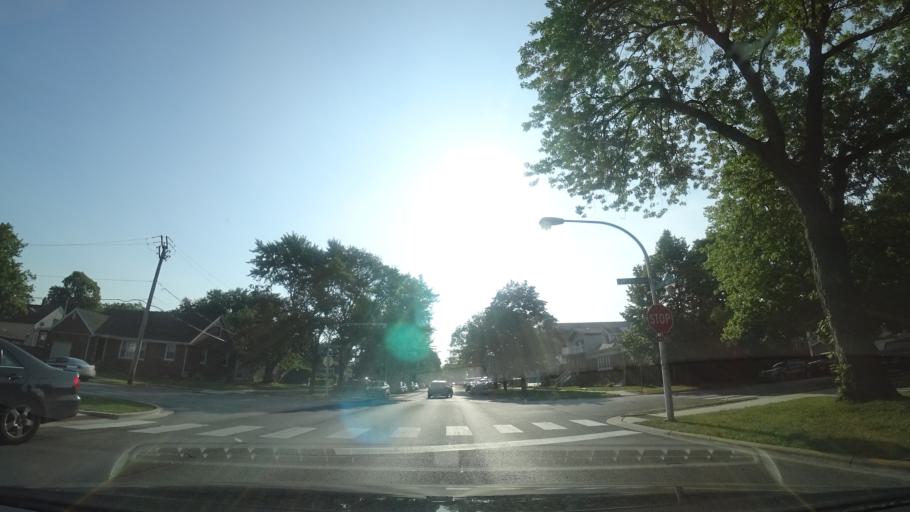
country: US
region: Illinois
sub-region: Cook County
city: Harwood Heights
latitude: 41.9624
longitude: -87.7602
